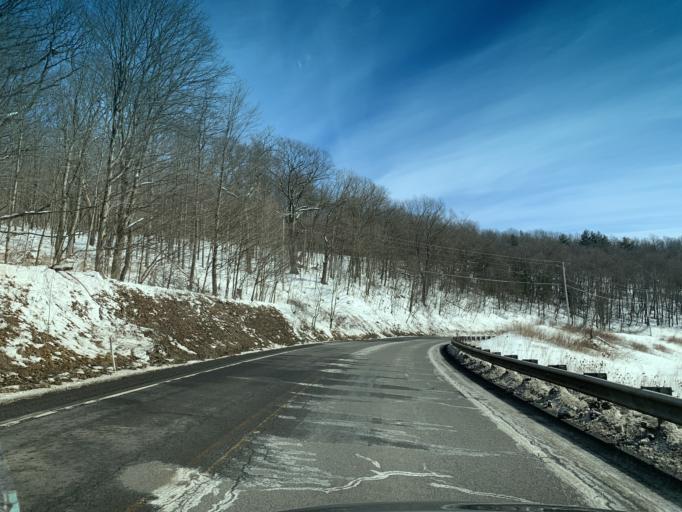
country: US
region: Maryland
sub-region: Allegany County
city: Lonaconing
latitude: 39.5964
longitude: -78.9439
